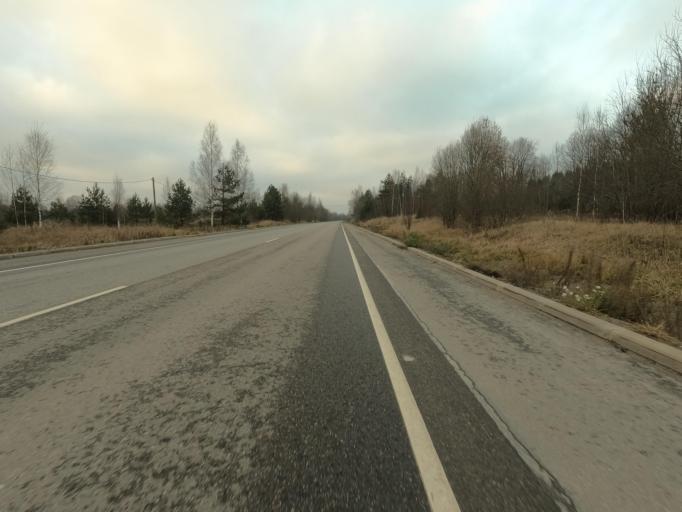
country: RU
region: Leningrad
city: Pavlovo
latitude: 59.8032
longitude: 30.9705
